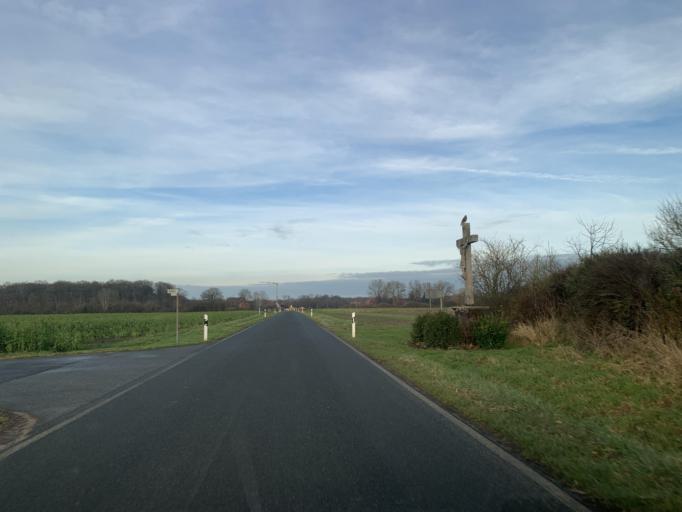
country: DE
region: North Rhine-Westphalia
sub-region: Regierungsbezirk Munster
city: Dulmen
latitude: 51.8297
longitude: 7.3562
